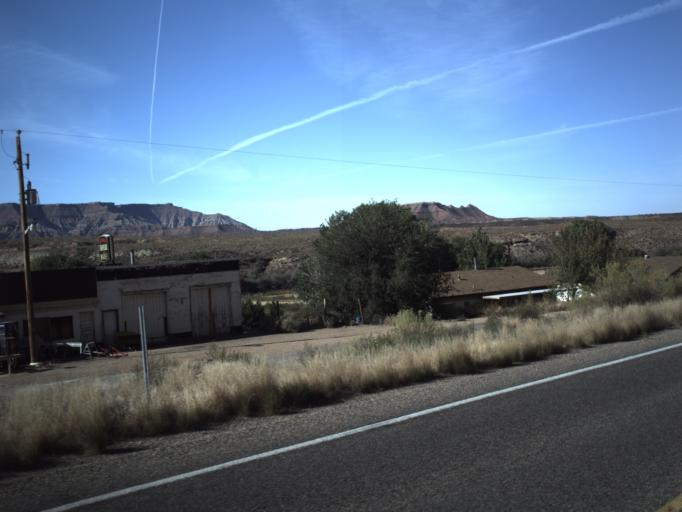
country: US
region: Utah
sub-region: Washington County
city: LaVerkin
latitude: 37.1952
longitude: -113.1535
